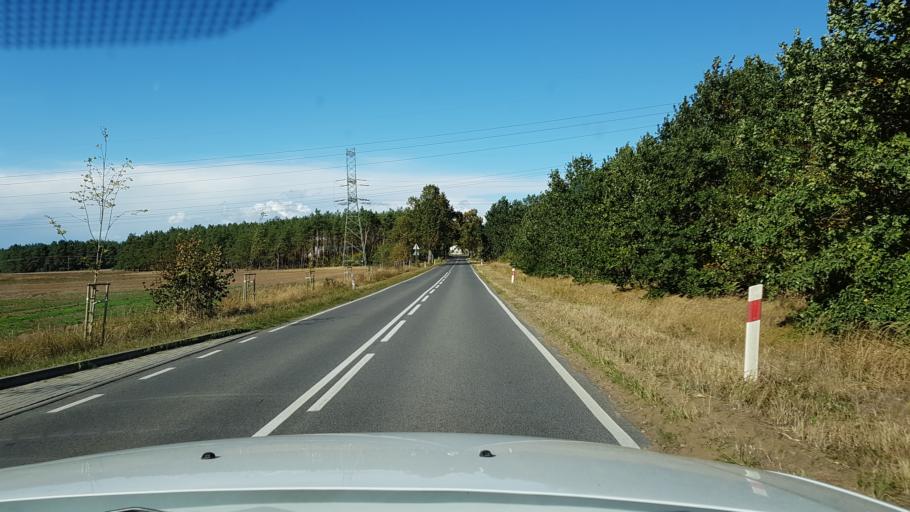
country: PL
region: West Pomeranian Voivodeship
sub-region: Powiat gryfinski
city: Gryfino
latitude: 53.2025
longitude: 14.5035
